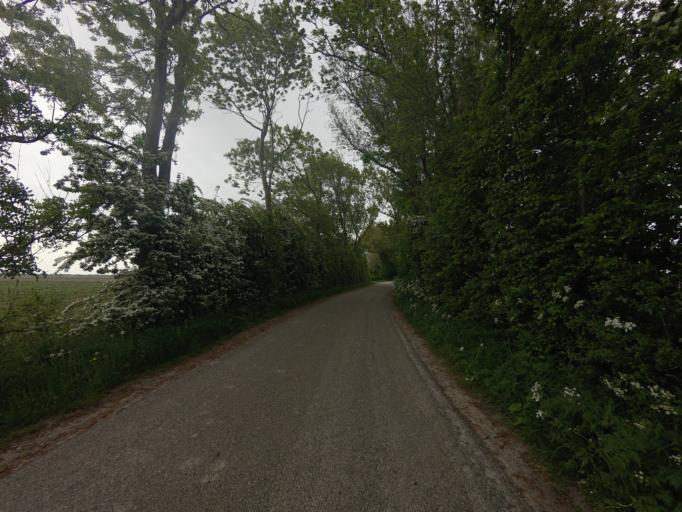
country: NL
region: Zeeland
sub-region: Gemeente Middelburg
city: Middelburg
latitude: 51.5260
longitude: 3.5718
